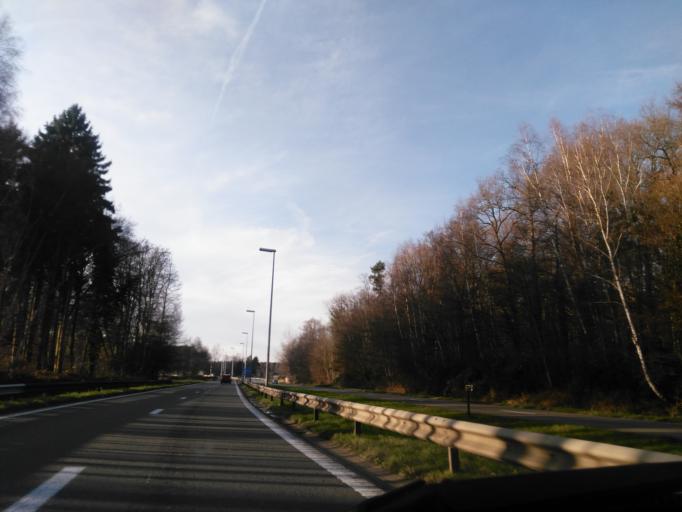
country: BE
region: Flanders
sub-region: Provincie Oost-Vlaanderen
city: Stekene
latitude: 51.2285
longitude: 4.0656
